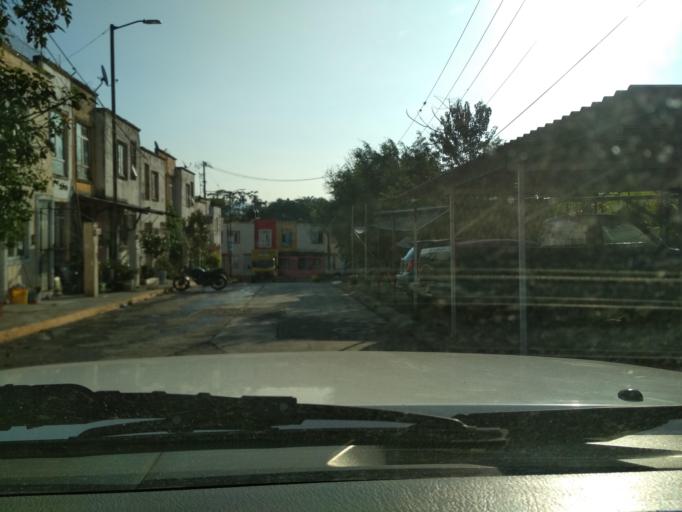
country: MX
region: Veracruz
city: Cordoba
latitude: 18.8685
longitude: -96.9335
